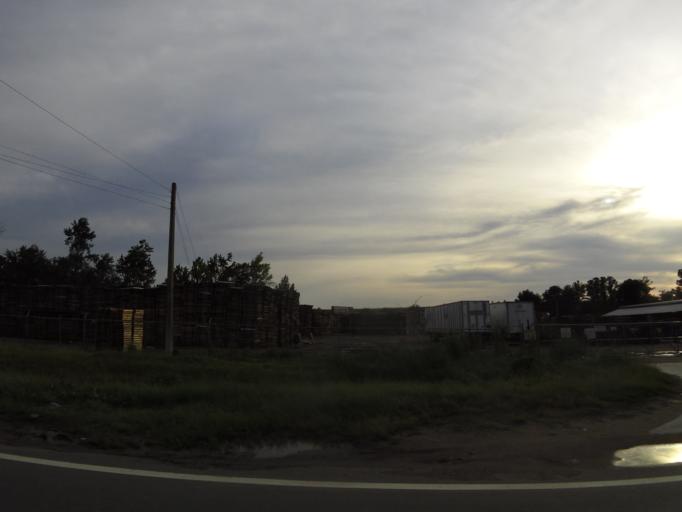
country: US
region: Florida
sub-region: Duval County
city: Jacksonville
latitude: 30.3991
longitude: -81.7538
